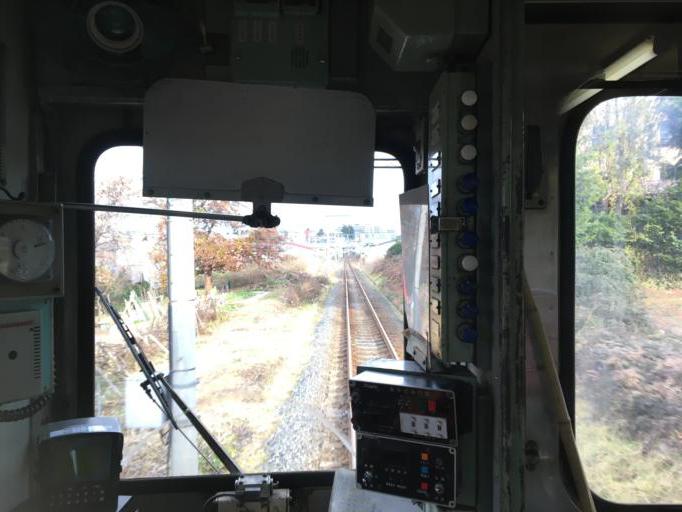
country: JP
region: Aomori
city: Hirosaki
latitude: 40.5889
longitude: 140.4691
